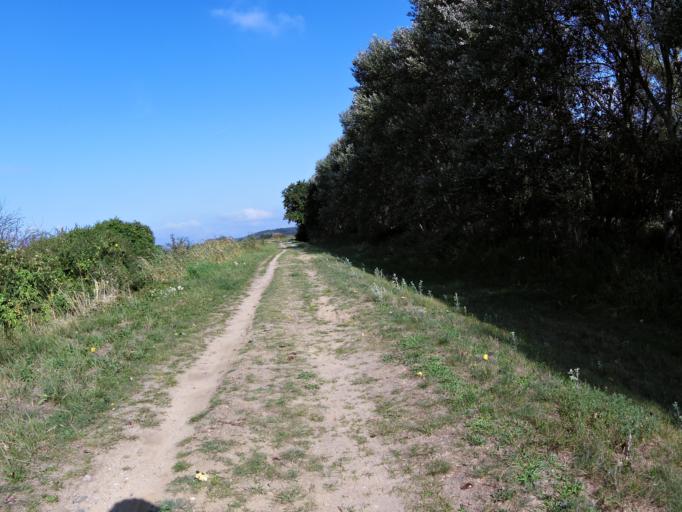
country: DE
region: Mecklenburg-Vorpommern
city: Loddin
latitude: 53.9826
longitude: 14.0484
